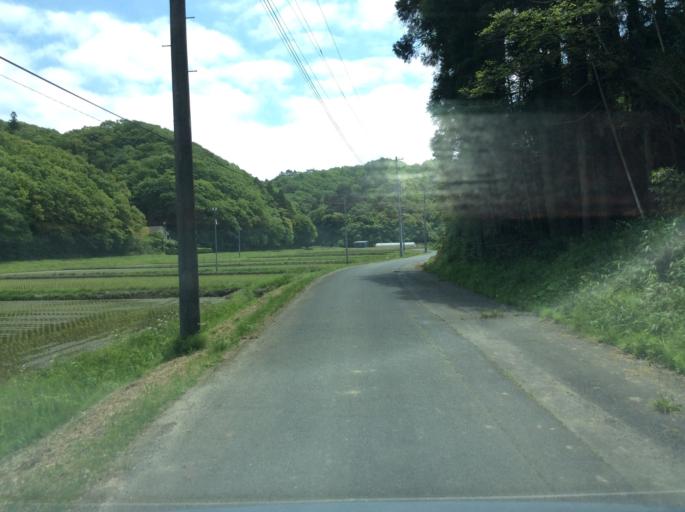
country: JP
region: Fukushima
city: Iwaki
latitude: 37.0111
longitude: 140.9441
